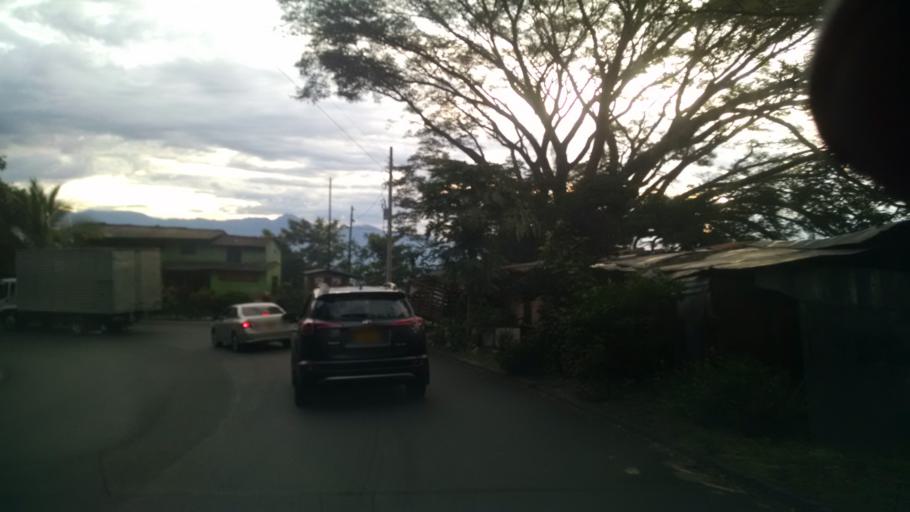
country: CO
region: Antioquia
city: Santa Barbara
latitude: 5.8457
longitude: -75.5794
